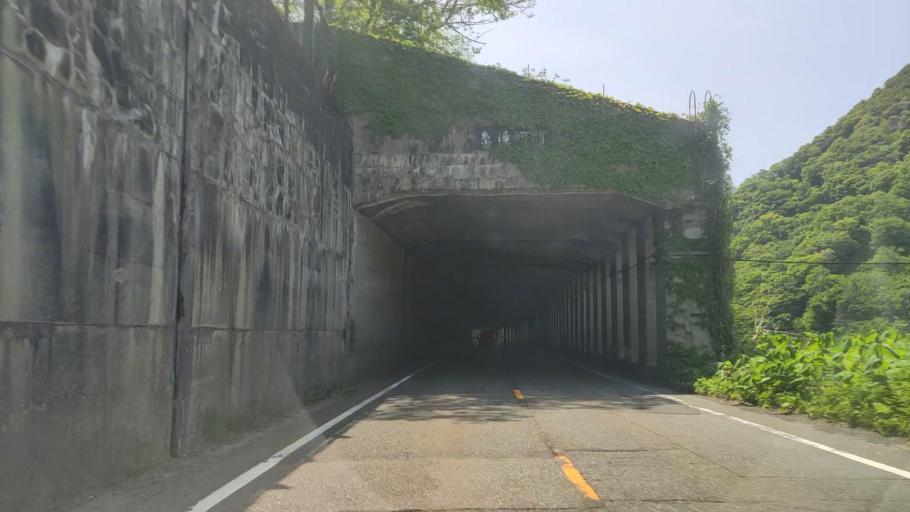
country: JP
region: Niigata
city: Itoigawa
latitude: 36.9558
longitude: 137.8608
